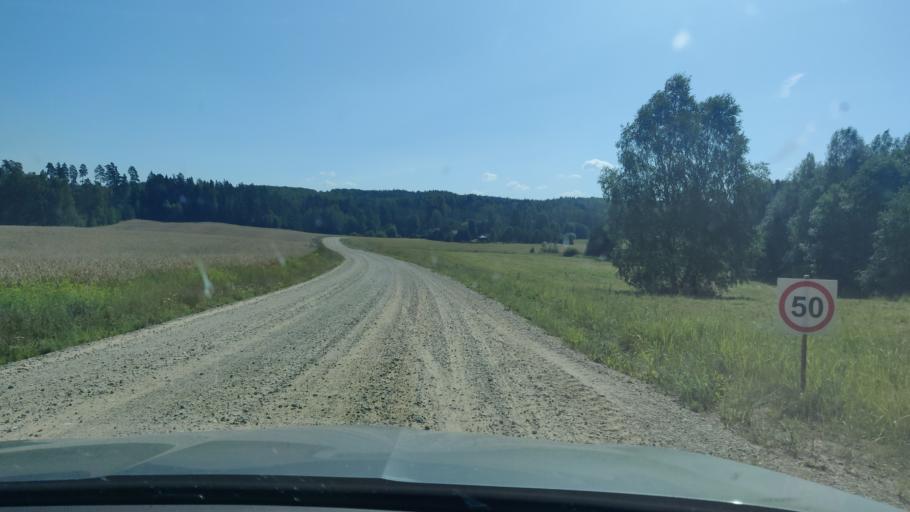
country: EE
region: Tartu
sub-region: Elva linn
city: Elva
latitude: 58.1339
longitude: 26.4019
